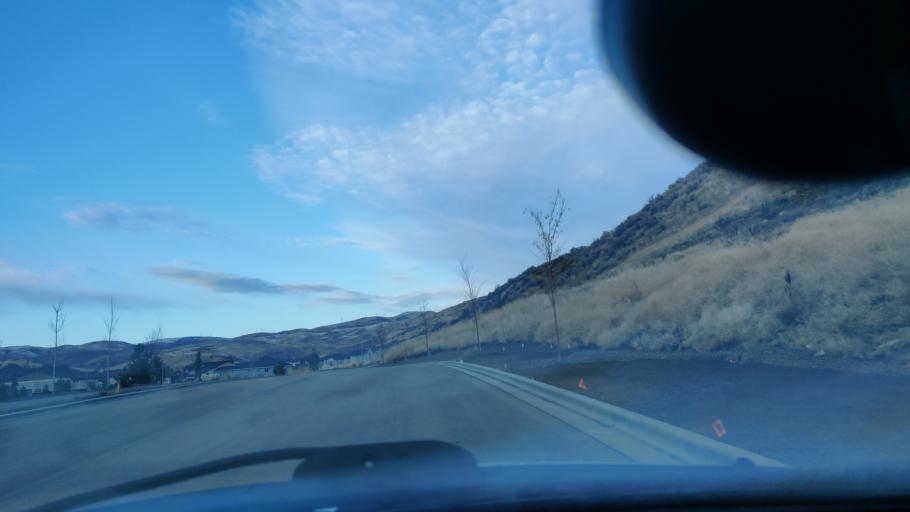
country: US
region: Idaho
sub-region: Ada County
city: Eagle
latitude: 43.7834
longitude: -116.2618
